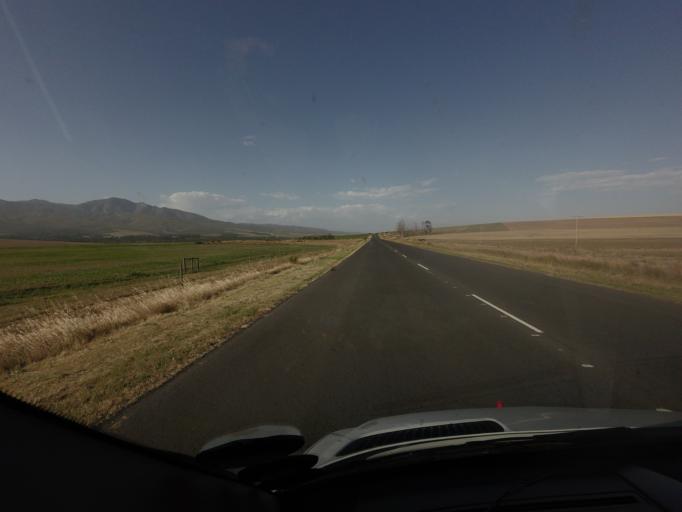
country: ZA
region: Western Cape
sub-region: Cape Winelands District Municipality
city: Ashton
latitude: -34.1503
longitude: 19.9746
